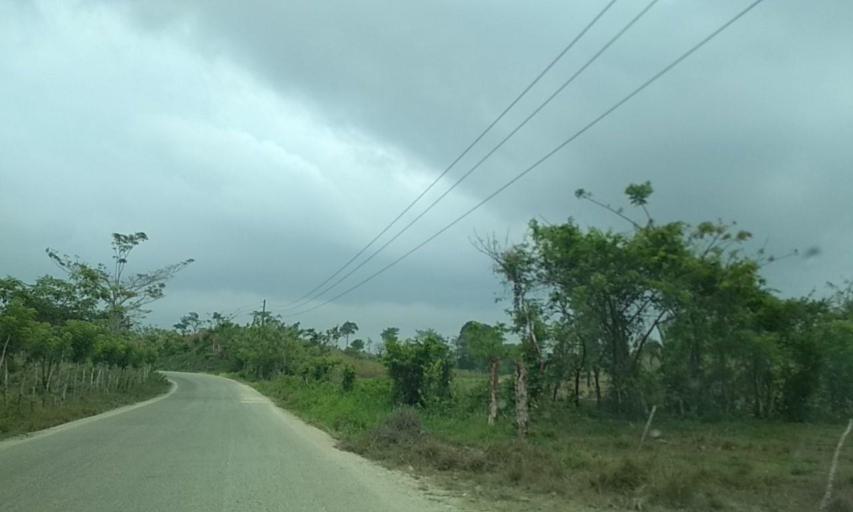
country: MX
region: Tabasco
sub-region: Huimanguillo
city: Francisco Rueda
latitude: 17.5999
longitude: -94.0901
